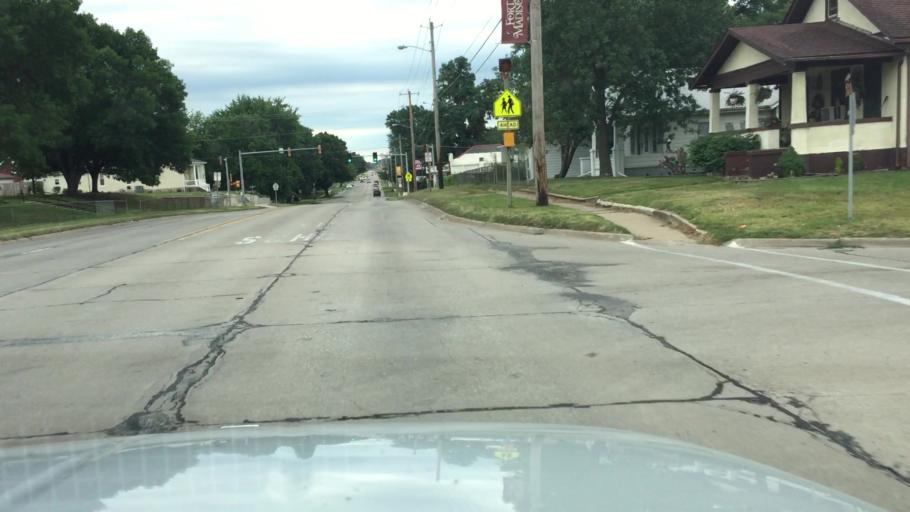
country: US
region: Iowa
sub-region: Lee County
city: Fort Madison
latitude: 40.6266
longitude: -91.3555
